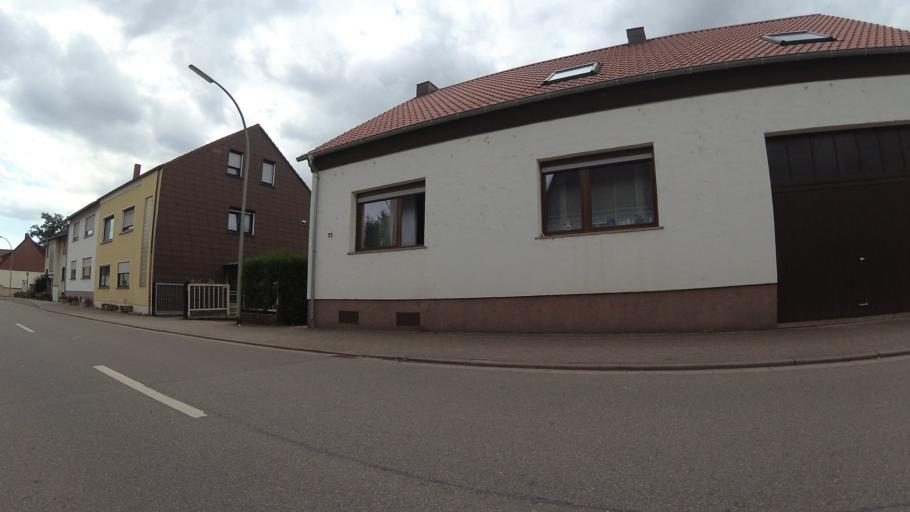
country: FR
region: Lorraine
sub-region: Departement de la Moselle
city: Sarreinsming
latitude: 49.1525
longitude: 7.1146
